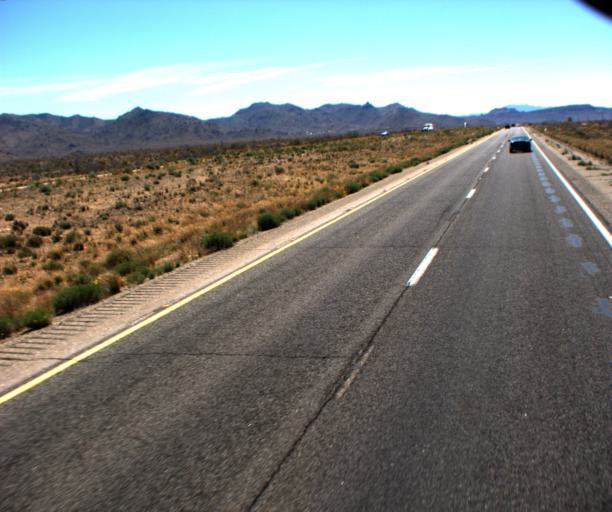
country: US
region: Arizona
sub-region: Mohave County
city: Golden Valley
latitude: 35.2916
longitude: -114.1834
